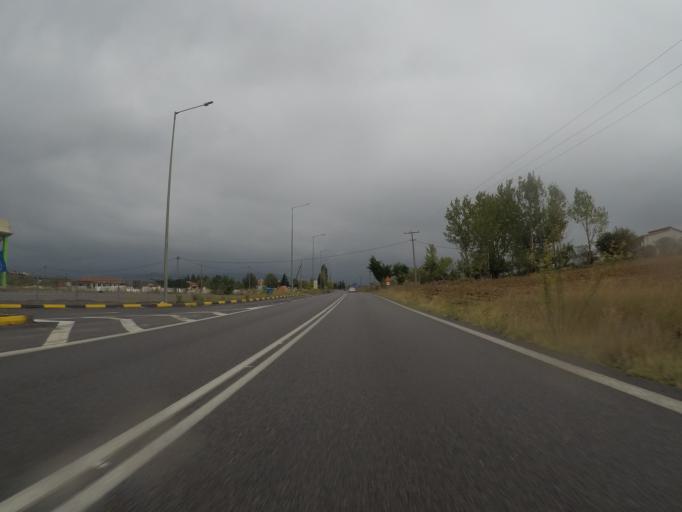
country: GR
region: Peloponnese
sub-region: Nomos Arkadias
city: Tripoli
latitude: 37.4754
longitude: 22.4037
